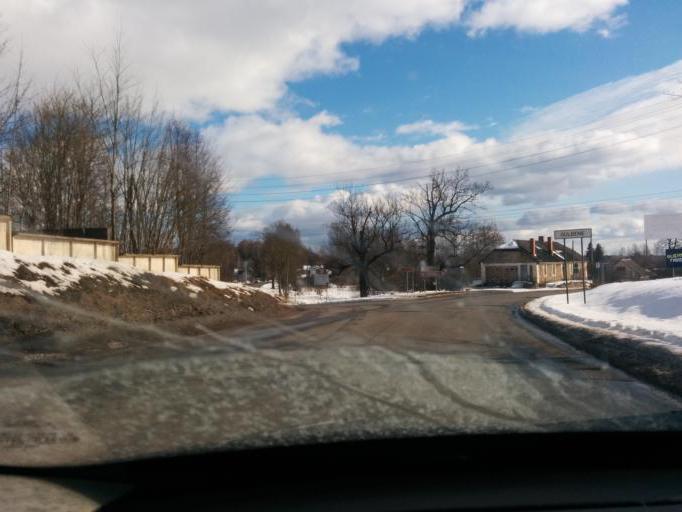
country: LV
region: Gulbenes Rajons
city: Gulbene
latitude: 57.1844
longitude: 26.7359
